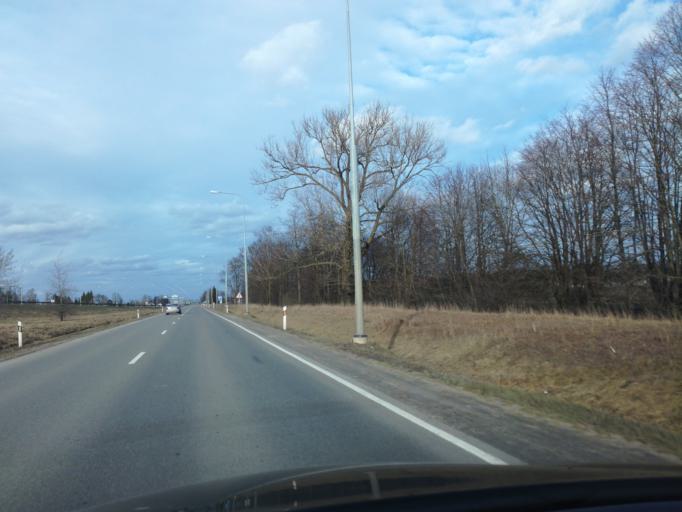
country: LT
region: Marijampoles apskritis
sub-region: Marijampole Municipality
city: Marijampole
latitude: 54.5838
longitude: 23.3800
